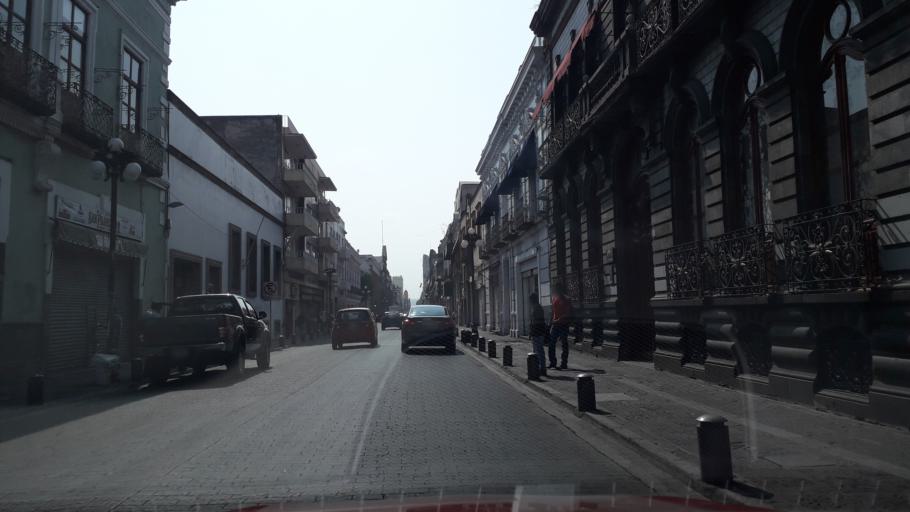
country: MX
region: Puebla
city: Puebla
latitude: 19.0480
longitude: -98.2057
